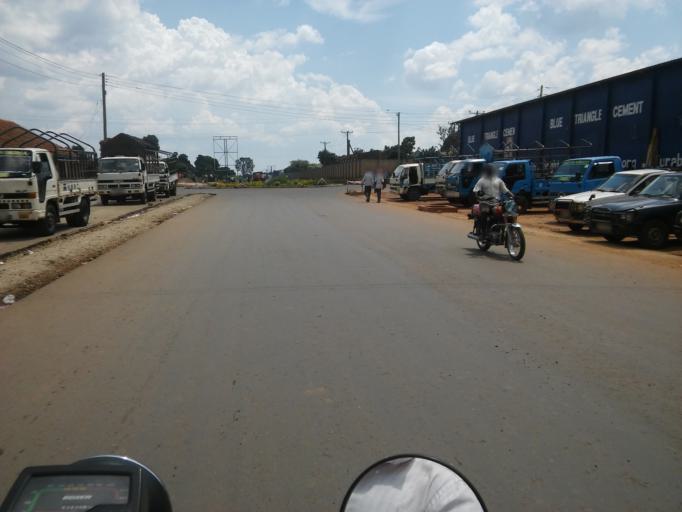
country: UG
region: Eastern Region
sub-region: Mbale District
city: Mbale
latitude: 1.0764
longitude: 34.1607
